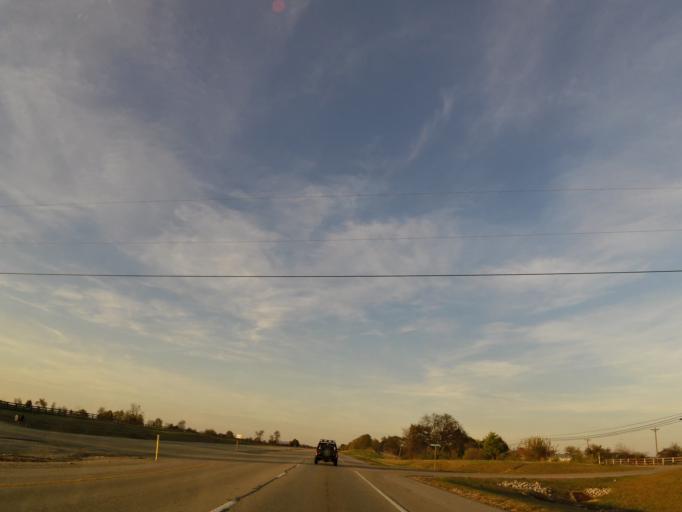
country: US
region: Kentucky
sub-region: Jessamine County
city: Nicholasville
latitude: 37.8029
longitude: -84.6014
